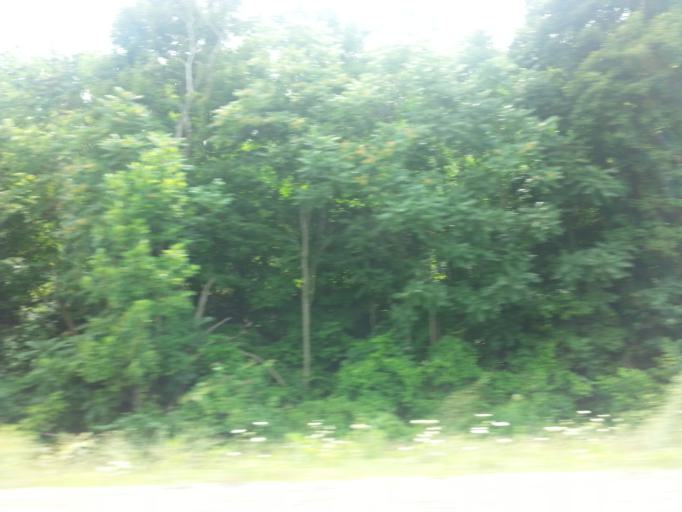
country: US
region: Tennessee
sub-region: Putnam County
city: Monterey
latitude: 36.1382
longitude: -85.3639
